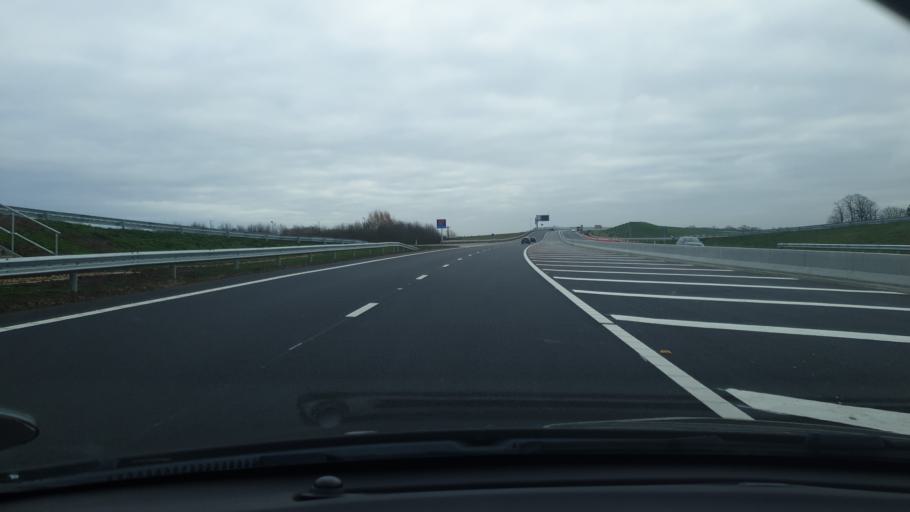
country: GB
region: England
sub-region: Cambridgeshire
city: Brampton
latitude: 52.3314
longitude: -0.2561
